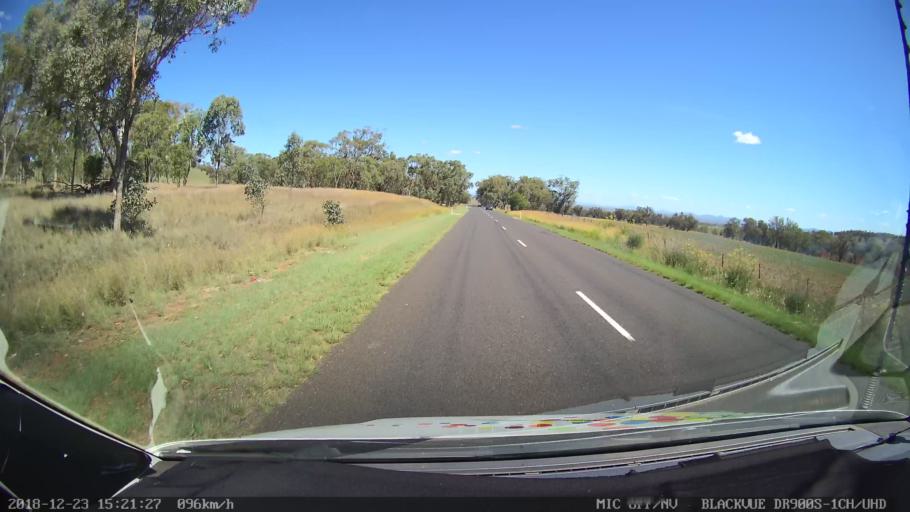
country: AU
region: New South Wales
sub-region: Tamworth Municipality
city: Manilla
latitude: -30.8566
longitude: 150.7967
